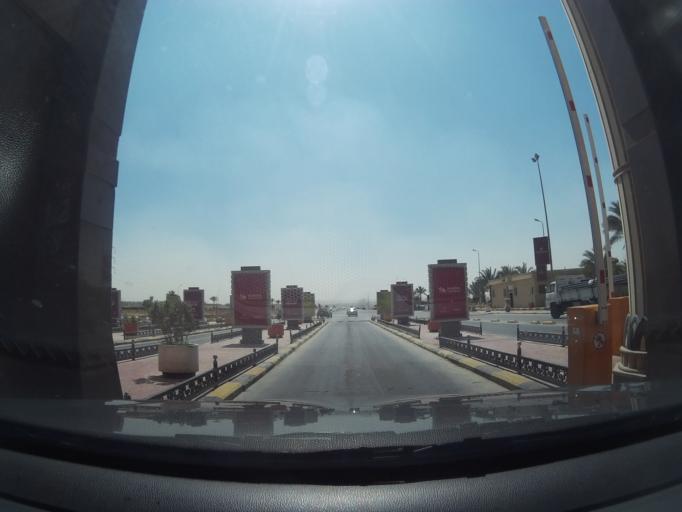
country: EG
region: As Suways
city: Ain Sukhna
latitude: 29.7657
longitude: 31.9485
